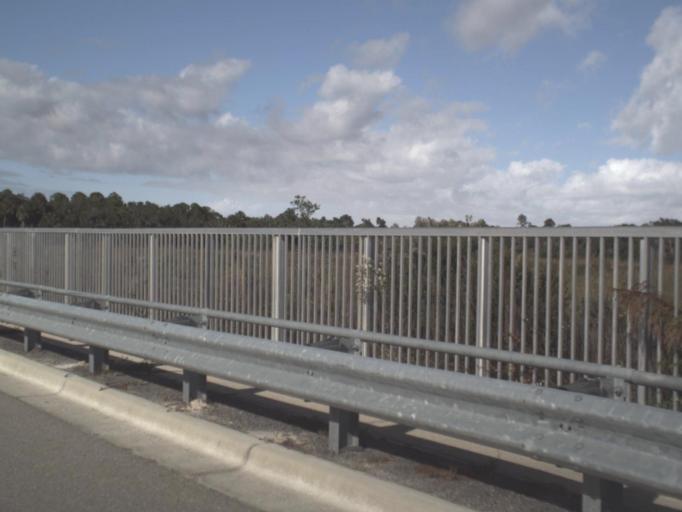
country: US
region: Florida
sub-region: Volusia County
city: Samsula-Spruce Creek
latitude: 29.0888
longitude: -81.0255
